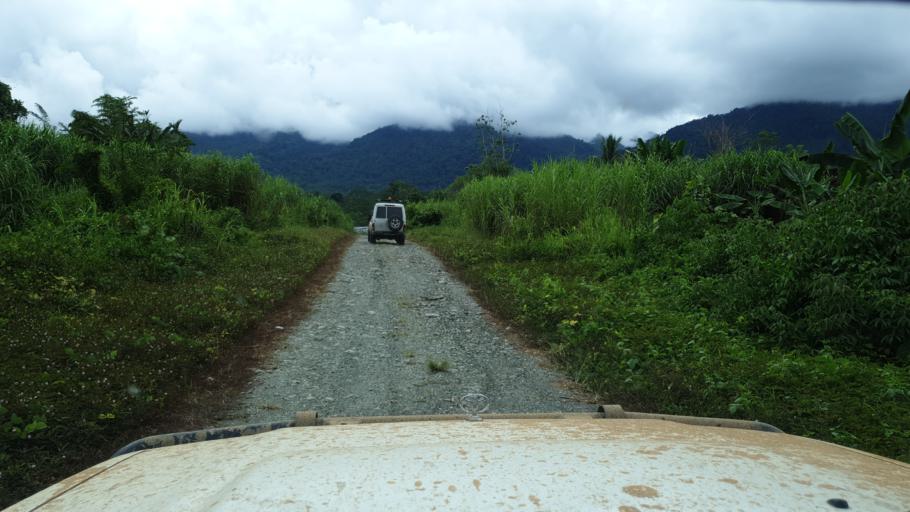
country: PG
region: Northern Province
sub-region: Sohe
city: Kokoda
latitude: -8.9398
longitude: 147.8676
